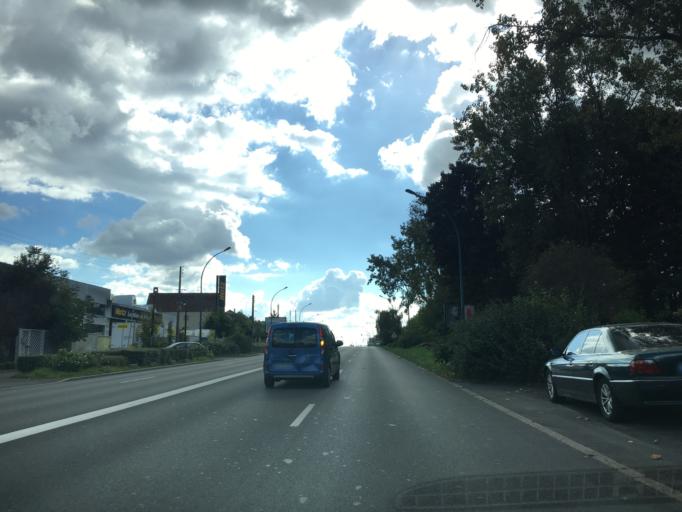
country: FR
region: Ile-de-France
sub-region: Departement des Hauts-de-Seine
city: Antony
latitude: 48.7354
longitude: 2.3013
